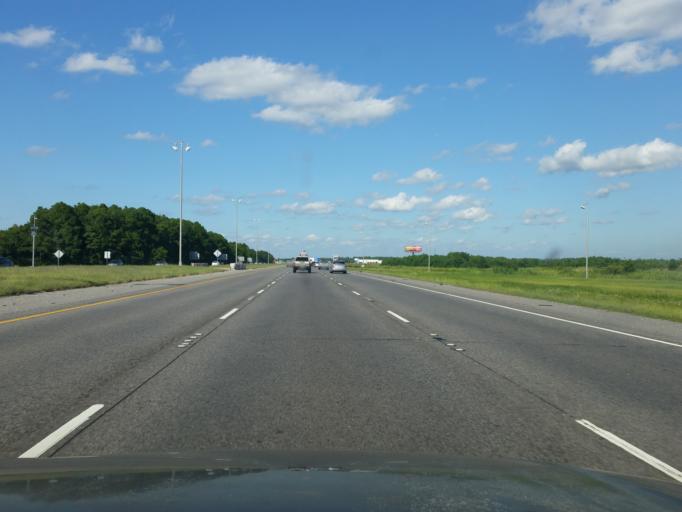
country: US
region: Louisiana
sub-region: Saint Tammany Parish
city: Eden Isle
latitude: 30.2242
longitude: -89.7807
